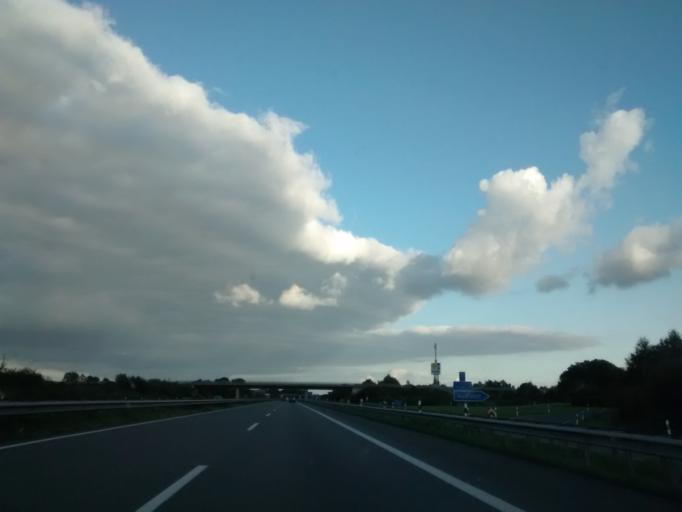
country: DE
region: Lower Saxony
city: Schuttorf
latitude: 52.3423
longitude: 7.2428
